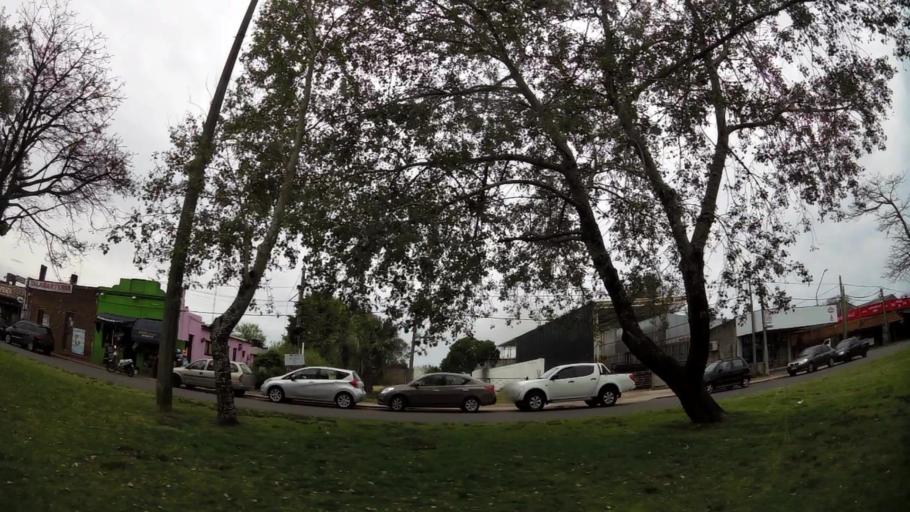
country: UY
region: Maldonado
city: Maldonado
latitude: -34.9054
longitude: -54.9633
